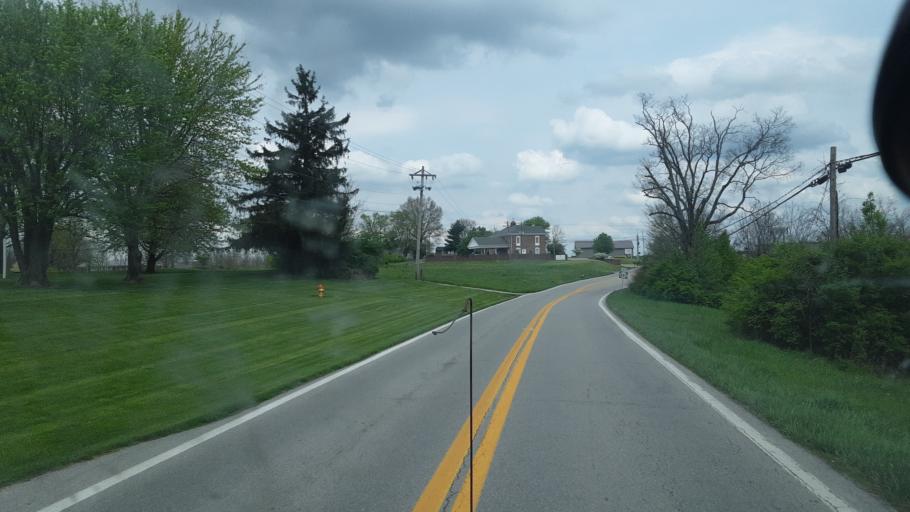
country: US
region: Kentucky
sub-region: Grant County
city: Dry Ridge
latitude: 38.6819
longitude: -84.6106
